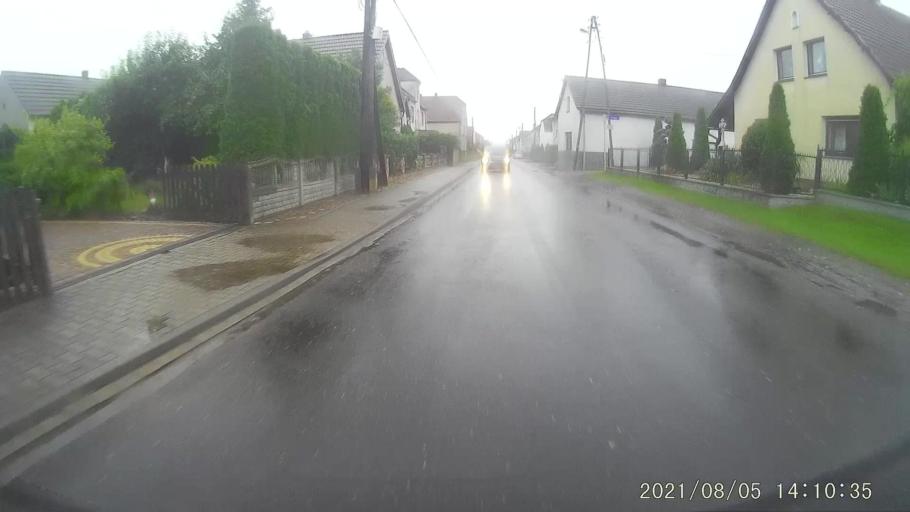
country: PL
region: Opole Voivodeship
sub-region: Powiat krapkowicki
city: Strzeleczki
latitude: 50.4716
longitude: 17.7875
